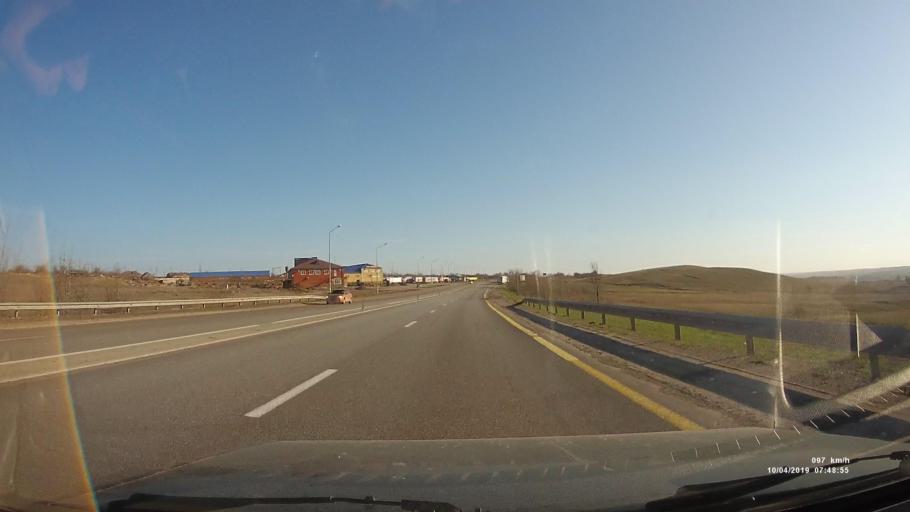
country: RU
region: Rostov
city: Kamensk-Shakhtinskiy
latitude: 48.2409
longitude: 40.2839
